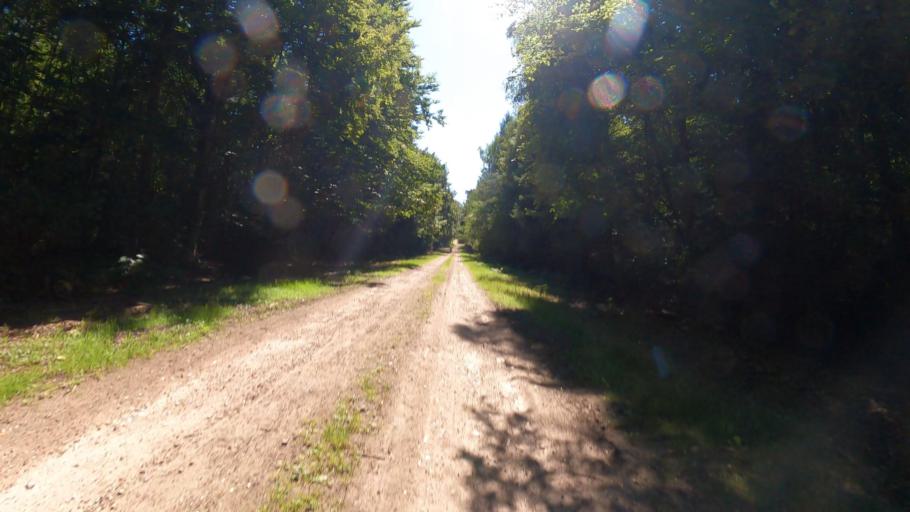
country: DE
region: Schleswig-Holstein
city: Aumuhle
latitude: 53.5155
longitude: 10.3376
